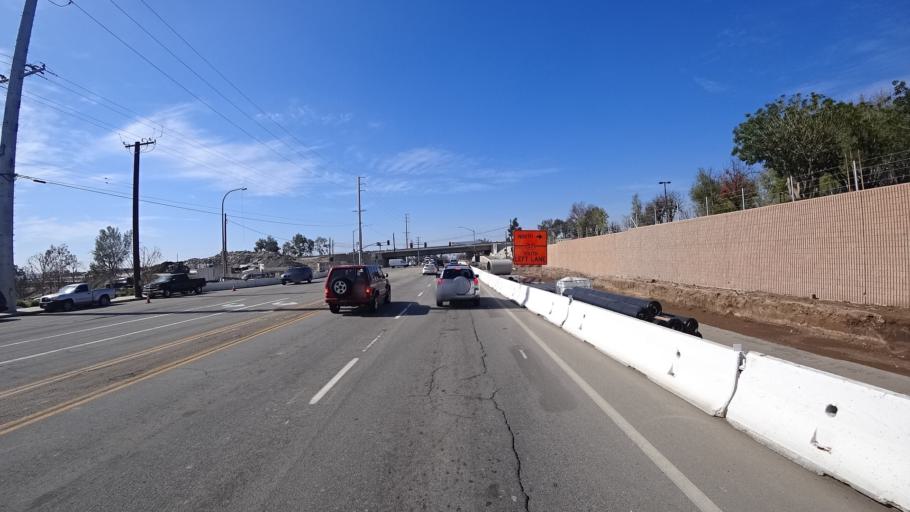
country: US
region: California
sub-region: Orange County
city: Brea
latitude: 33.9255
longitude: -117.8780
